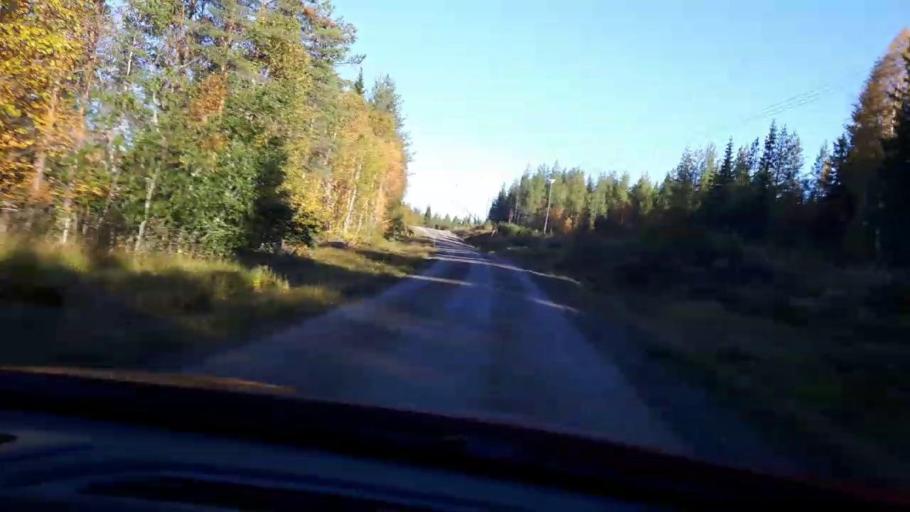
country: SE
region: Jaemtland
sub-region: Stroemsunds Kommun
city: Stroemsund
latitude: 64.3720
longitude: 15.1555
